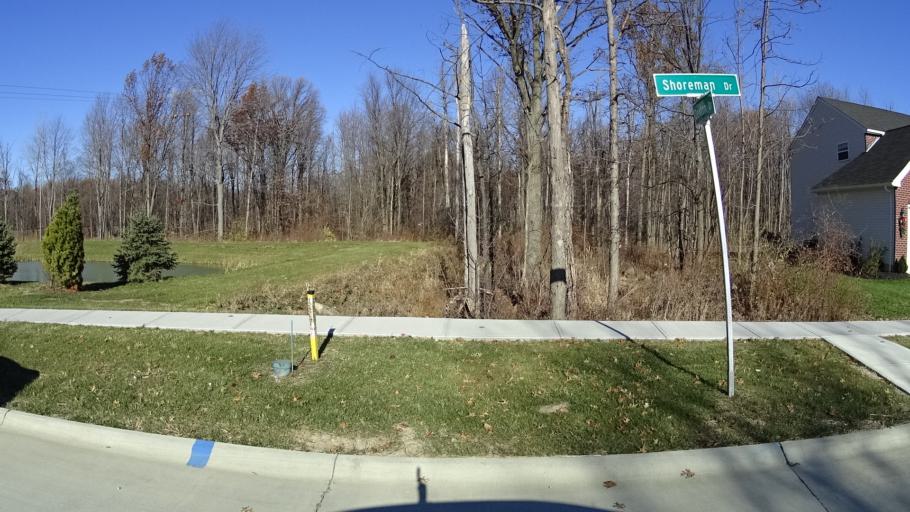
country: US
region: Ohio
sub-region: Lorain County
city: Avon
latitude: 41.4375
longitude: -82.0663
